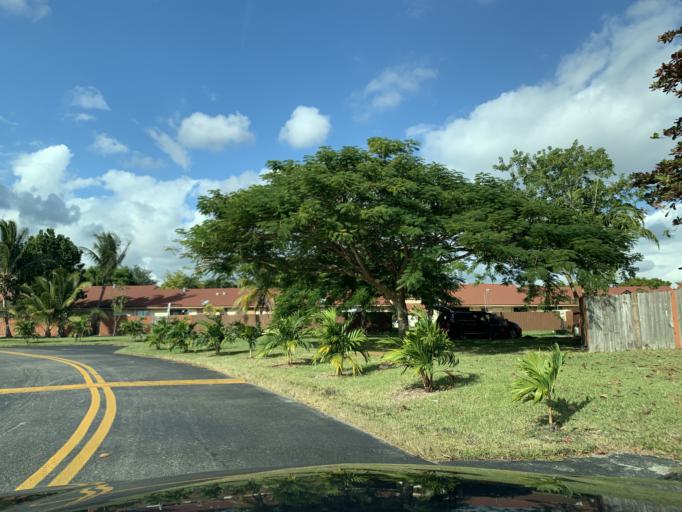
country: US
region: Florida
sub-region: Miami-Dade County
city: Naranja
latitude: 25.5058
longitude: -80.4179
